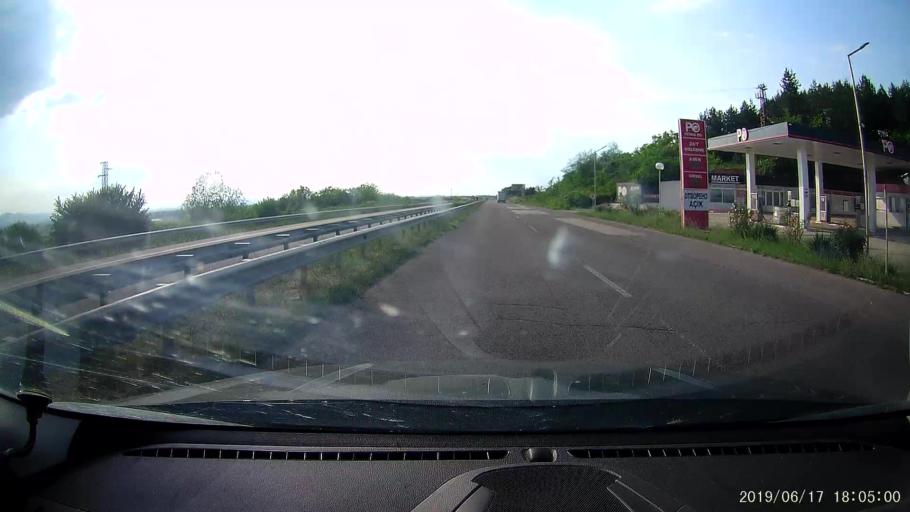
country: BG
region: Khaskovo
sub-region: Obshtina Svilengrad
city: Svilengrad
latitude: 41.7927
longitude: 26.1857
